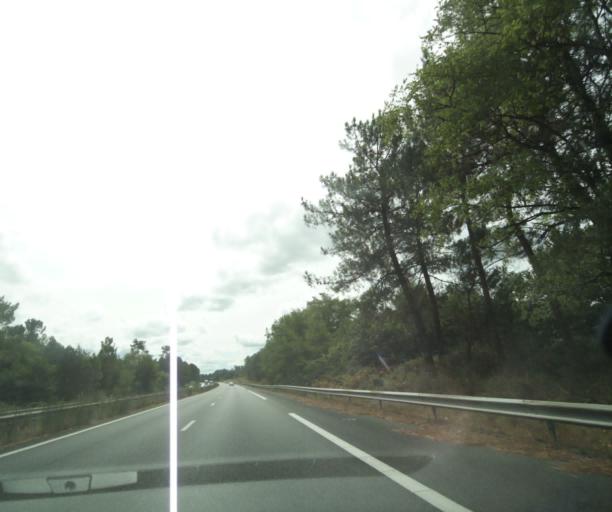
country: FR
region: Aquitaine
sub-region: Departement de la Gironde
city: Marcillac
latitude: 45.2643
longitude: -0.5481
